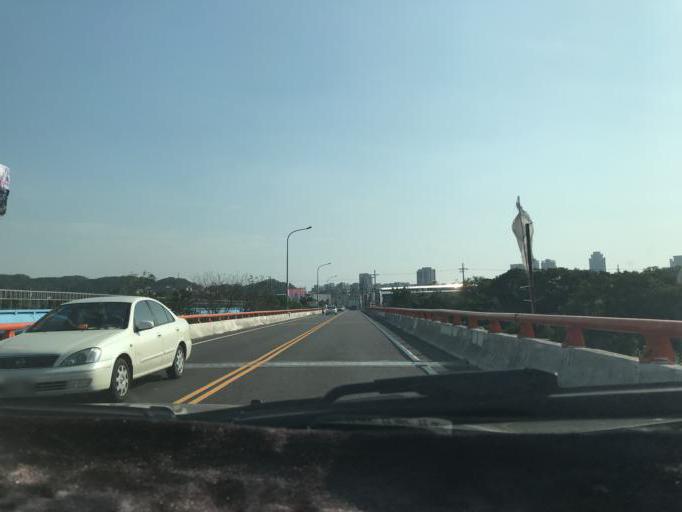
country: TW
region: Taiwan
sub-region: Hsinchu
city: Zhubei
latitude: 24.8376
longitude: 121.0363
